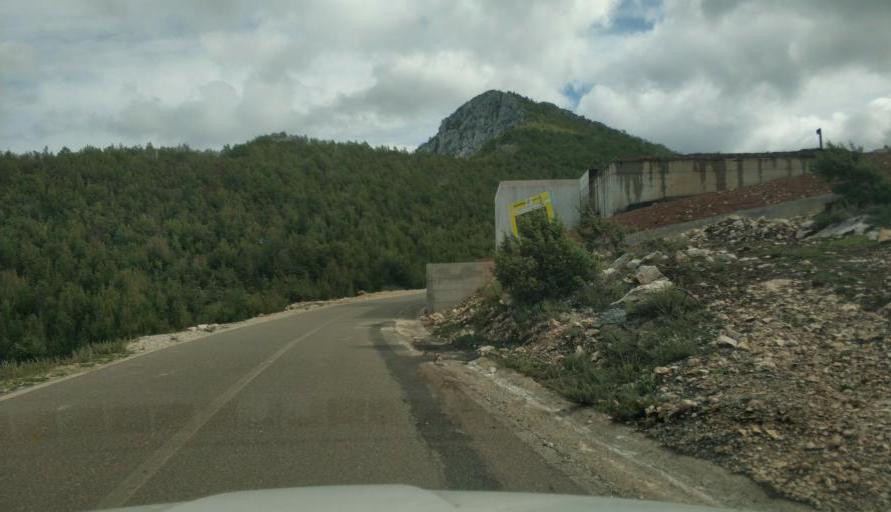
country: AL
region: Durres
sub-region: Rrethi i Krujes
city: Kruje
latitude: 41.5254
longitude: 19.7998
